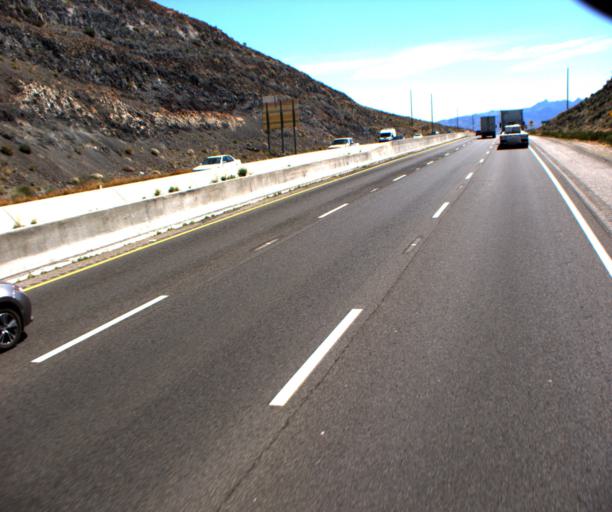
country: US
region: Arizona
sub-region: Mohave County
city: Kingman
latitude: 35.2091
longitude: -114.1039
